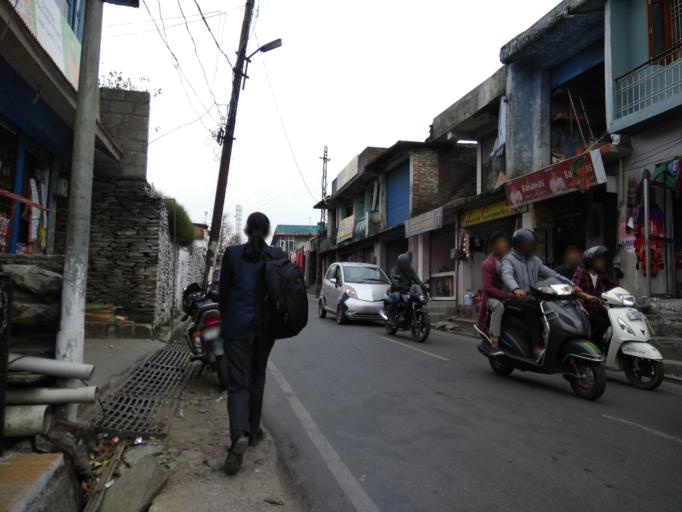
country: IN
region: Himachal Pradesh
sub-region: Kangra
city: Dharmsala
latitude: 32.1837
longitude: 76.3730
